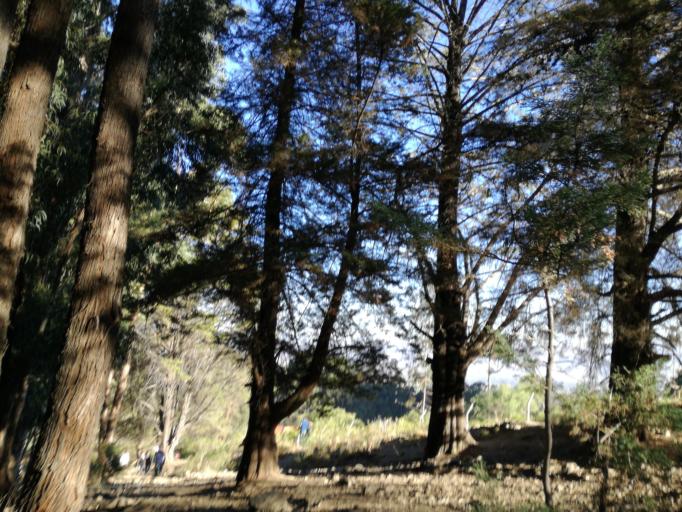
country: BO
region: Cochabamba
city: Sipe Sipe
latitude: -17.3414
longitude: -66.3332
